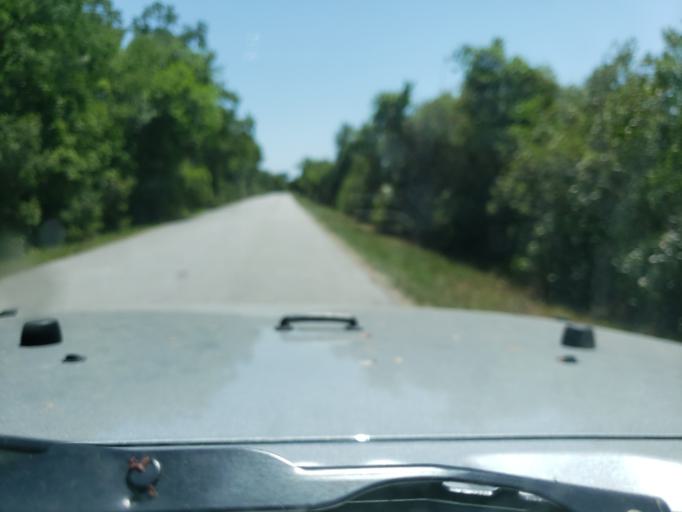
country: US
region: Georgia
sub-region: Chatham County
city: Thunderbolt
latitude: 32.0759
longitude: -81.0436
